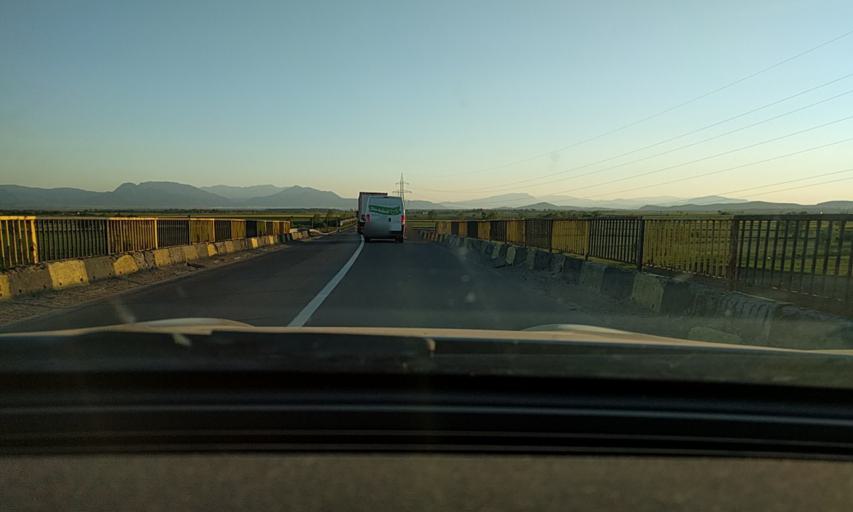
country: RO
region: Covasna
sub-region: Comuna Ozun
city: Ozun
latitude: 45.7891
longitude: 25.8334
